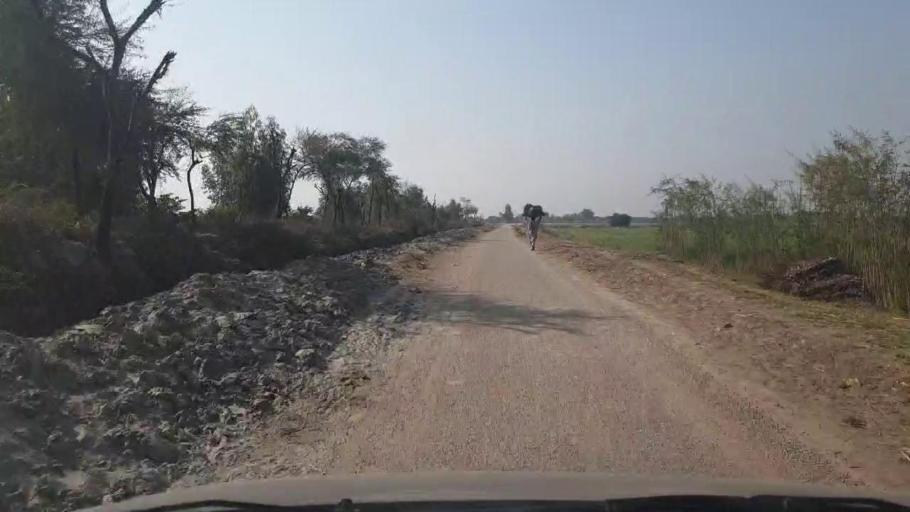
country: PK
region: Sindh
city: Mirwah Gorchani
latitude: 25.2625
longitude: 69.1138
